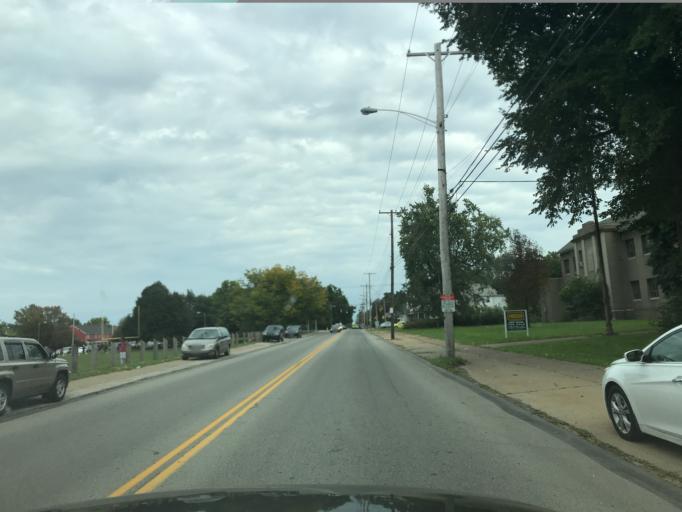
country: US
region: Pennsylvania
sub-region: Erie County
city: Wesleyville
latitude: 42.1302
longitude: -80.0393
